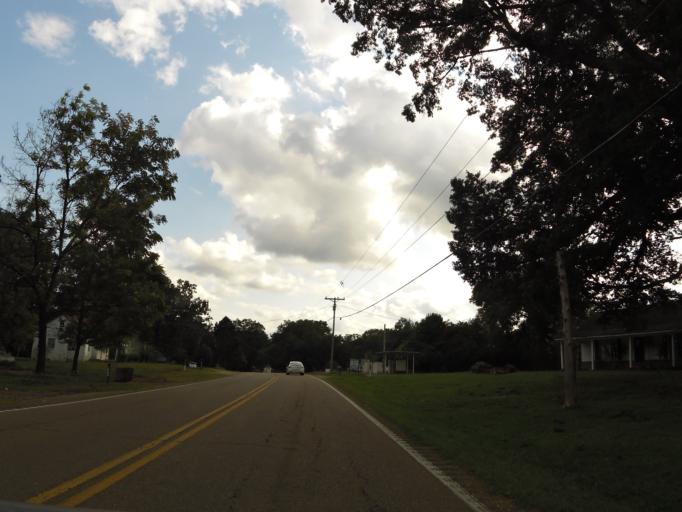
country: US
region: Mississippi
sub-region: Alcorn County
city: Farmington
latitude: 35.0098
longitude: -88.4592
